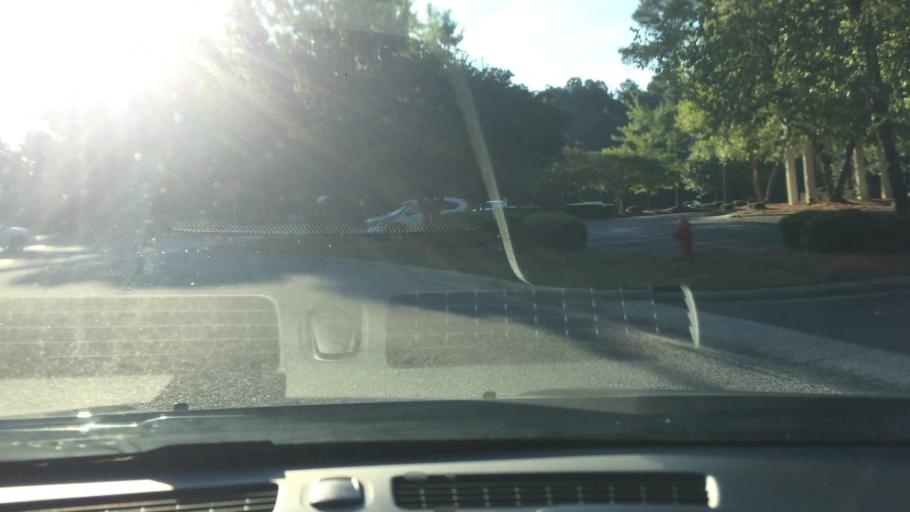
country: US
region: North Carolina
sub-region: Pitt County
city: Summerfield
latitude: 35.6030
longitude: -77.4057
